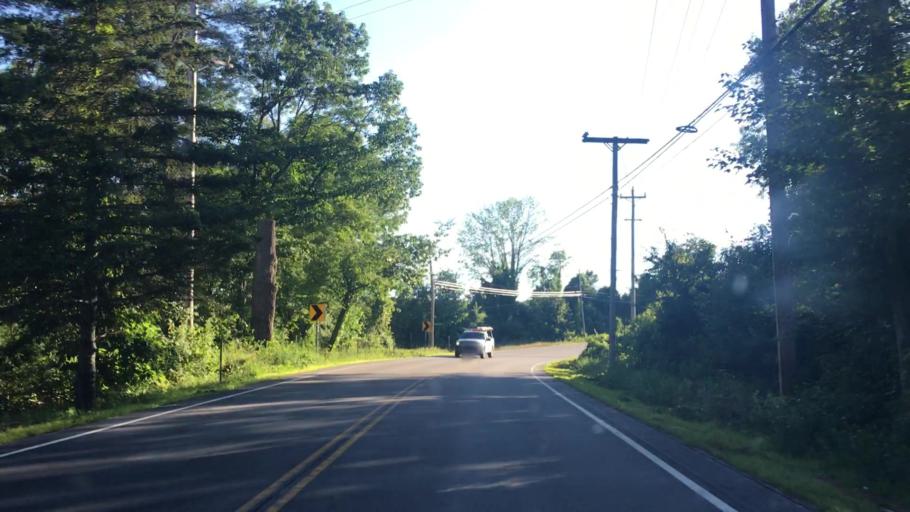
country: US
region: New Hampshire
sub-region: Rockingham County
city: Chester
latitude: 42.9524
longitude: -71.2360
